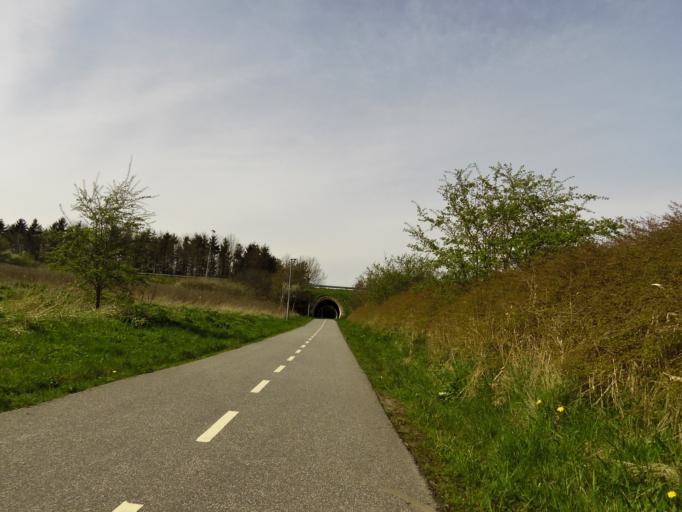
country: DK
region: Central Jutland
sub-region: Skive Kommune
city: Skive
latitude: 56.5799
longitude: 9.0259
